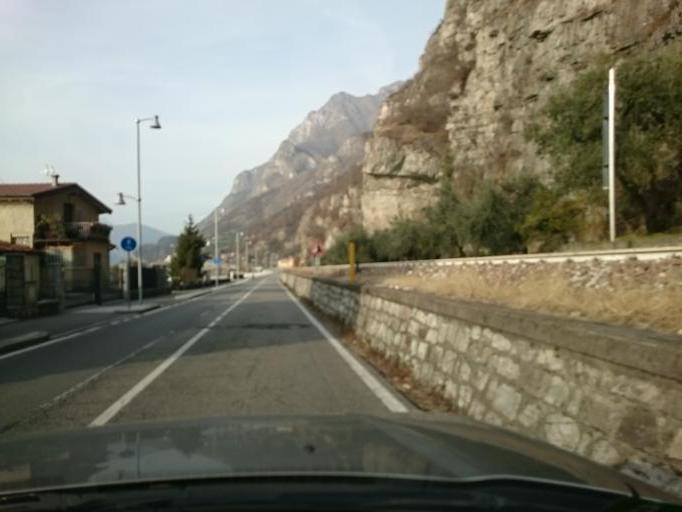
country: IT
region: Lombardy
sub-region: Provincia di Brescia
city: Marone
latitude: 45.7454
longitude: 10.0896
